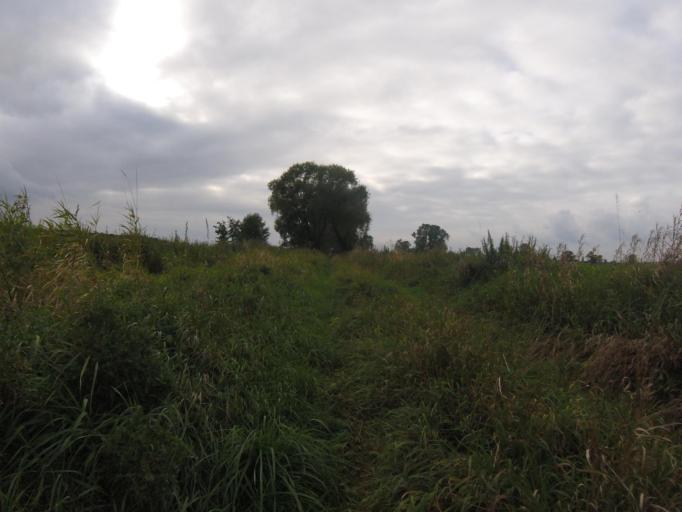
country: DE
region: Brandenburg
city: Mittenwalde
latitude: 52.2614
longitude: 13.5007
